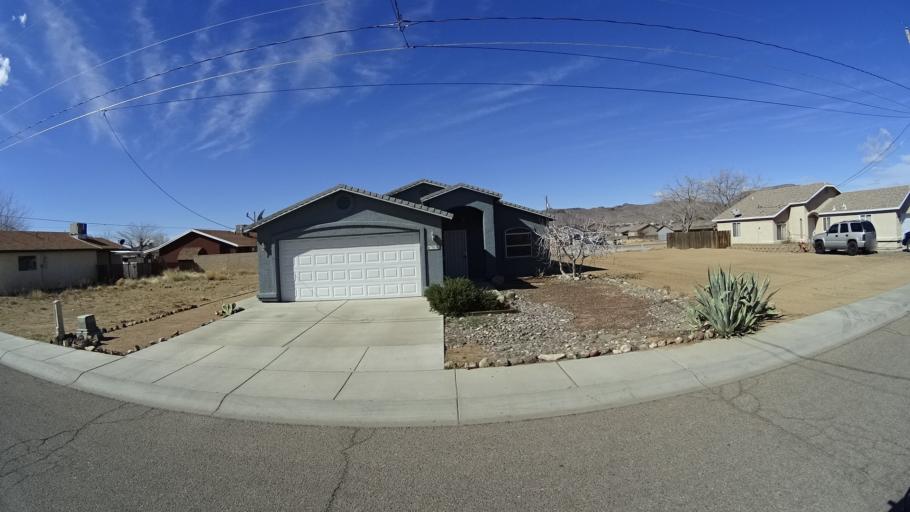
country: US
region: Arizona
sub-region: Mohave County
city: New Kingman-Butler
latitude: 35.2288
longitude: -114.0182
